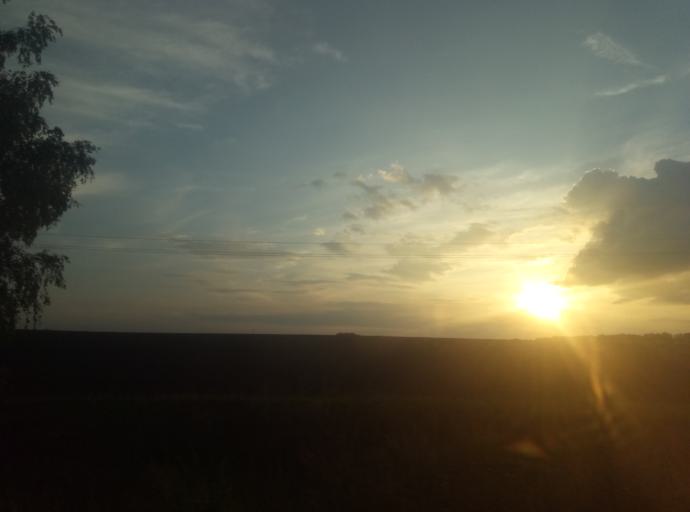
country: RU
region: Tula
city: Kireyevsk
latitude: 53.8635
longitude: 37.8813
